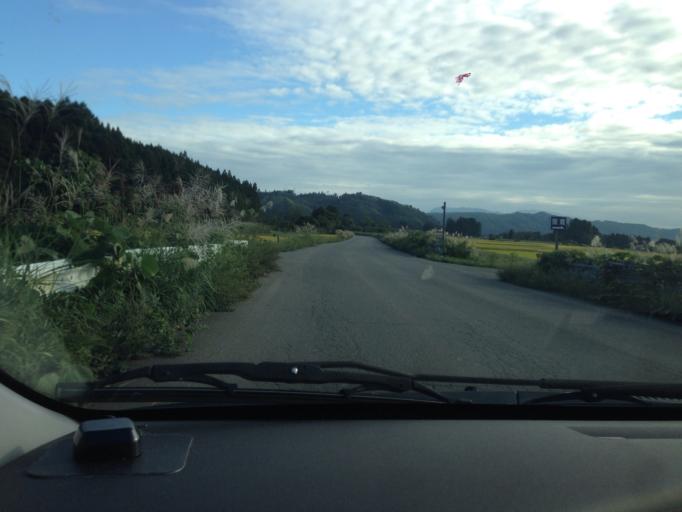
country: JP
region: Fukushima
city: Kitakata
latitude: 37.5906
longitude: 139.7737
